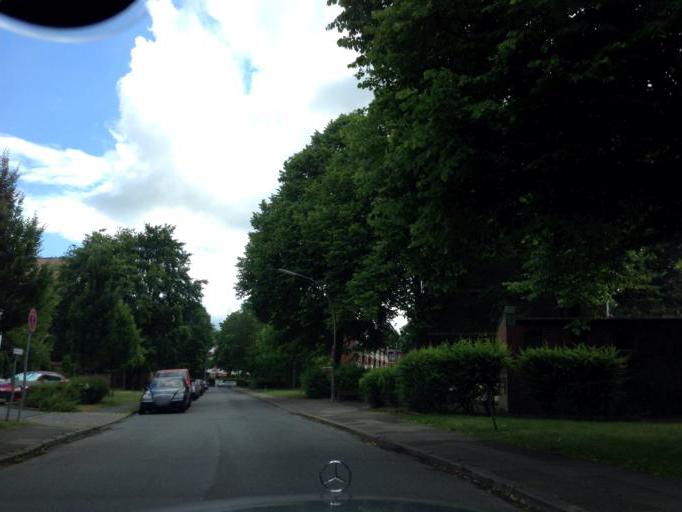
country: DE
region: Schleswig-Holstein
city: Barsbuettel
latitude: 53.5832
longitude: 10.1524
